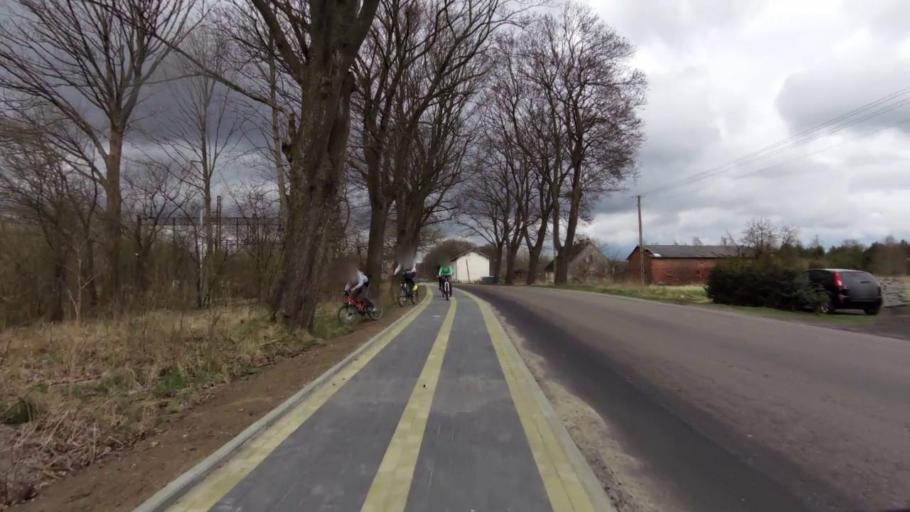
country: PL
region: West Pomeranian Voivodeship
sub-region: Powiat koszalinski
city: Sianow
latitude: 54.2476
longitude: 16.3030
